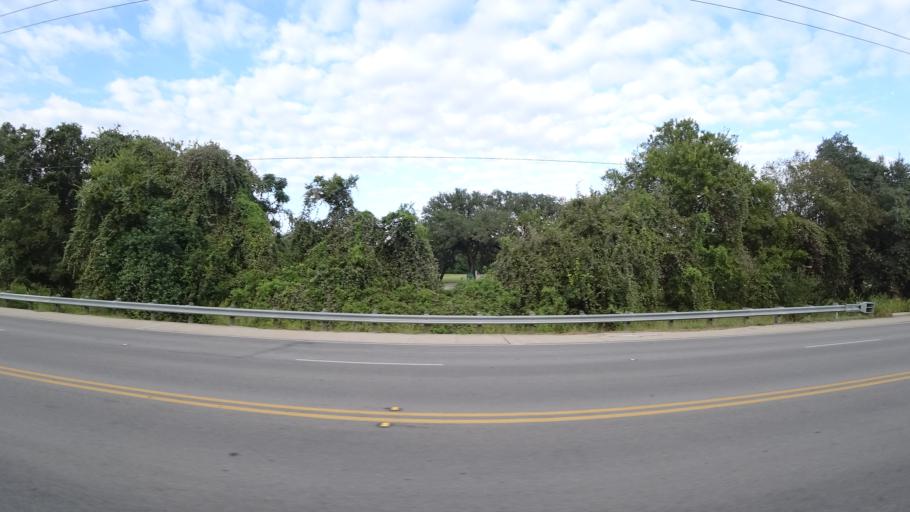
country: US
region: Texas
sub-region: Travis County
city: Rollingwood
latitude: 30.2870
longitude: -97.7797
